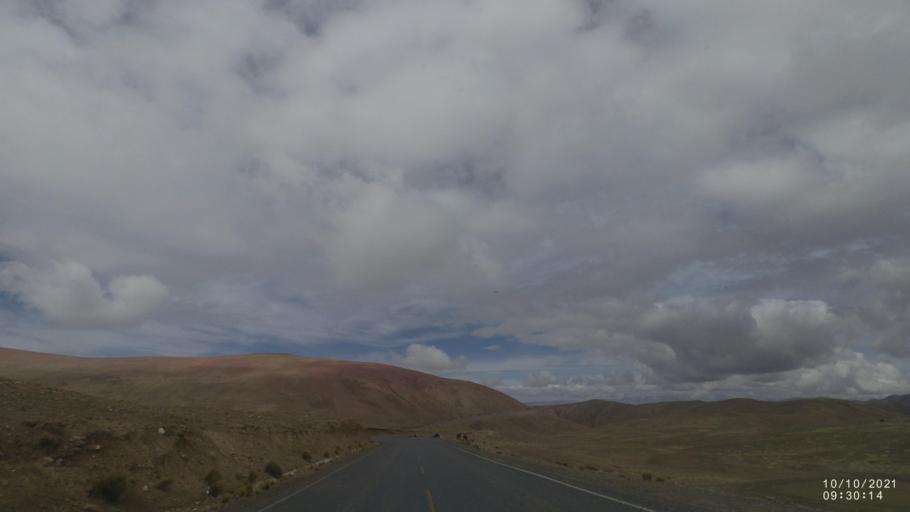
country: BO
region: La Paz
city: Quime
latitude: -17.1191
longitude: -67.3282
